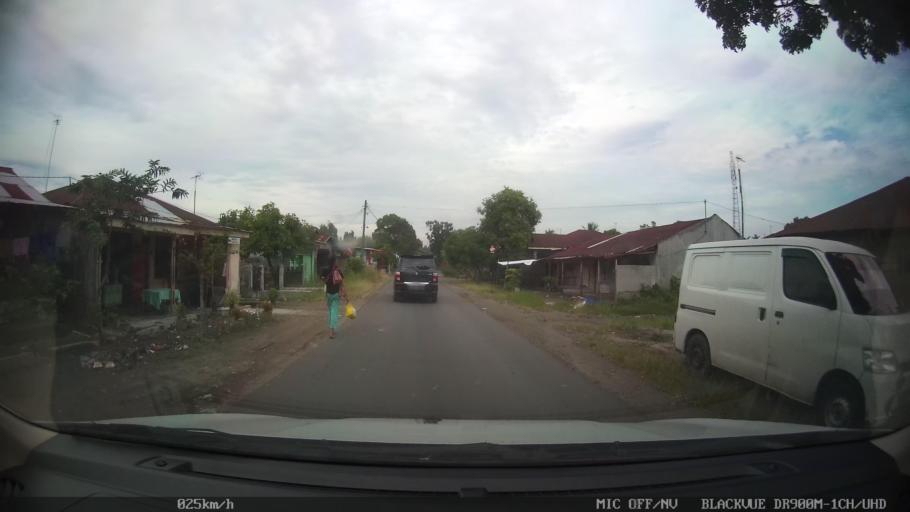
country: ID
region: North Sumatra
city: Sunggal
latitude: 3.6625
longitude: 98.5915
